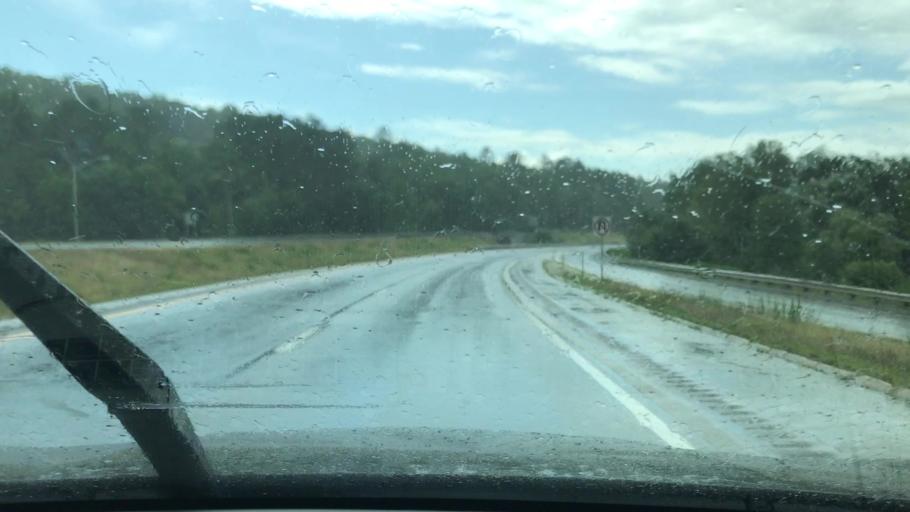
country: US
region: New Hampshire
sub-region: Grafton County
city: Littleton
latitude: 44.2961
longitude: -71.7699
